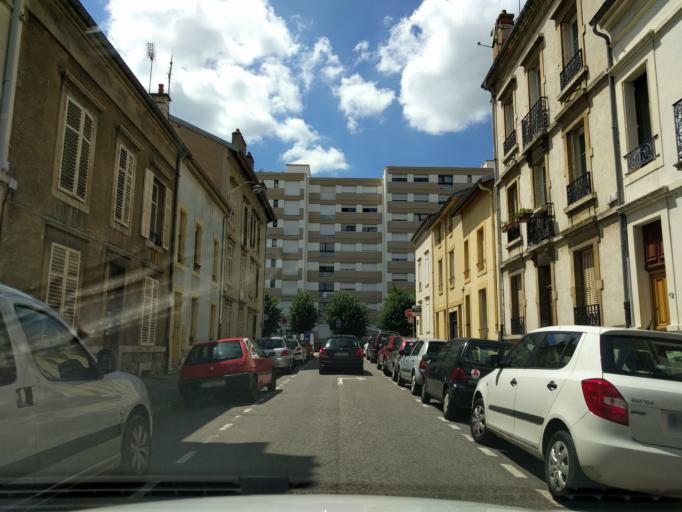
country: FR
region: Lorraine
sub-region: Departement de Meurthe-et-Moselle
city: Laxou
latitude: 48.6879
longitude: 6.1618
